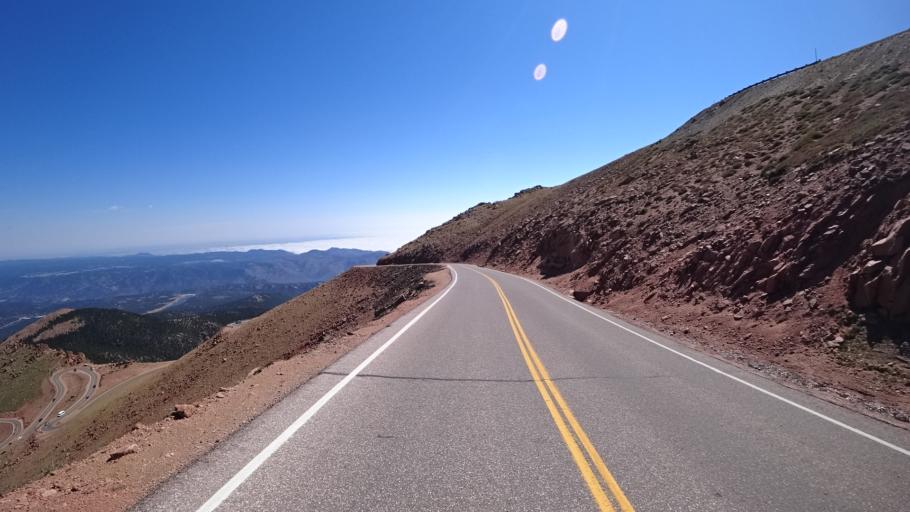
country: US
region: Colorado
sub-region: El Paso County
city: Cascade-Chipita Park
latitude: 38.8656
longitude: -105.0684
